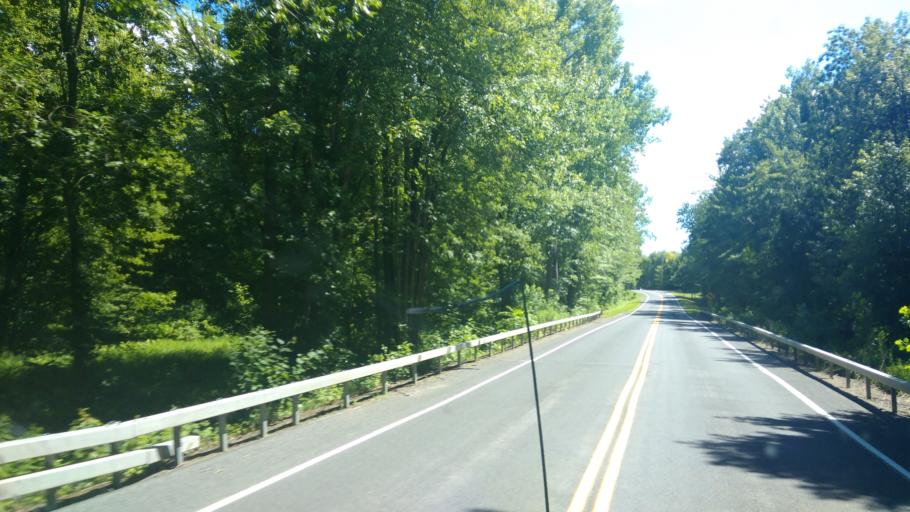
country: US
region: New York
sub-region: Wayne County
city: Sodus
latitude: 43.1908
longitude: -77.0497
